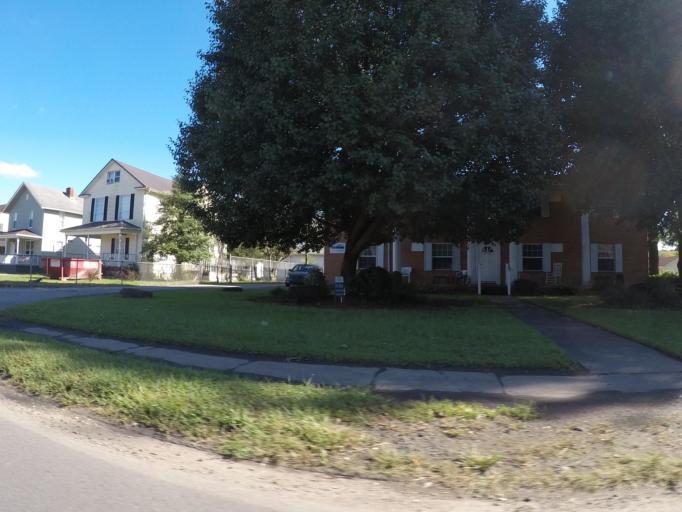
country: US
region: Ohio
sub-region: Lawrence County
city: Burlington
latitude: 38.4086
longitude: -82.4921
